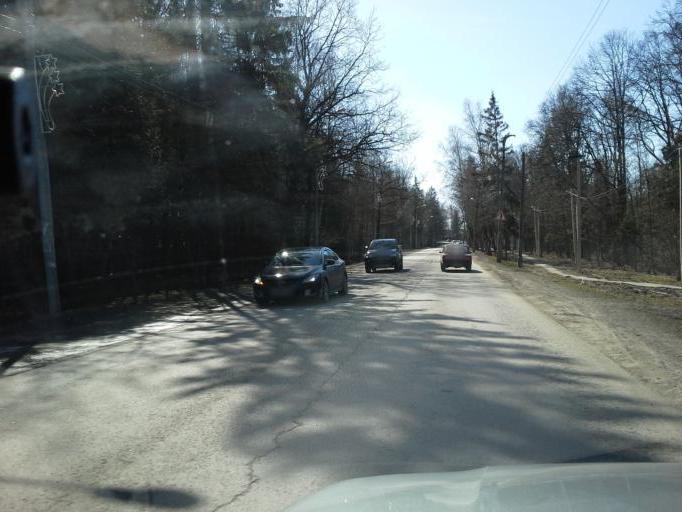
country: RU
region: Moskovskaya
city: Odintsovo
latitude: 55.6394
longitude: 37.2617
